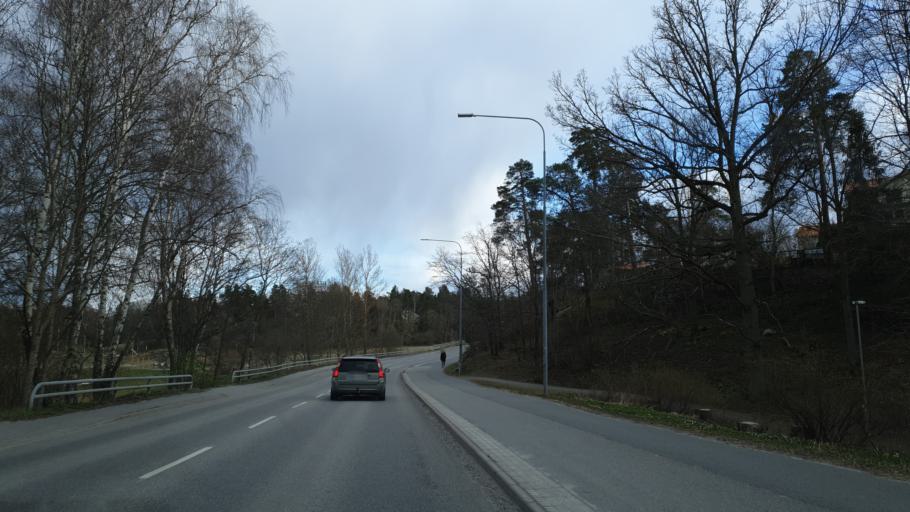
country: SE
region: Stockholm
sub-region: Lidingo
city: Lidingoe
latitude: 59.3740
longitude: 18.1318
